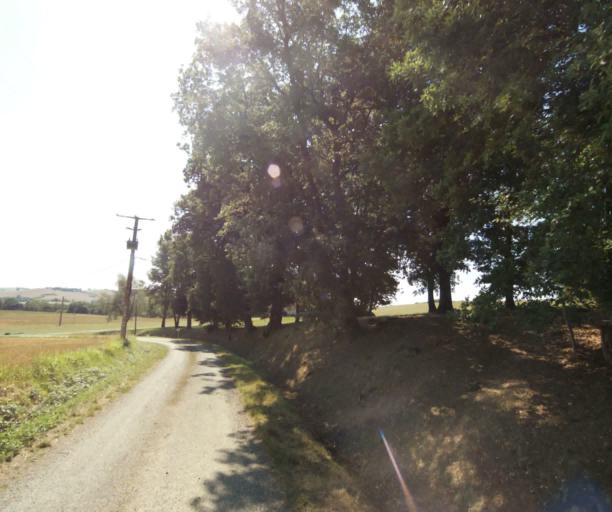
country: FR
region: Midi-Pyrenees
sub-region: Departement de l'Ariege
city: Lezat-sur-Leze
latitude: 43.2927
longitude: 1.3345
